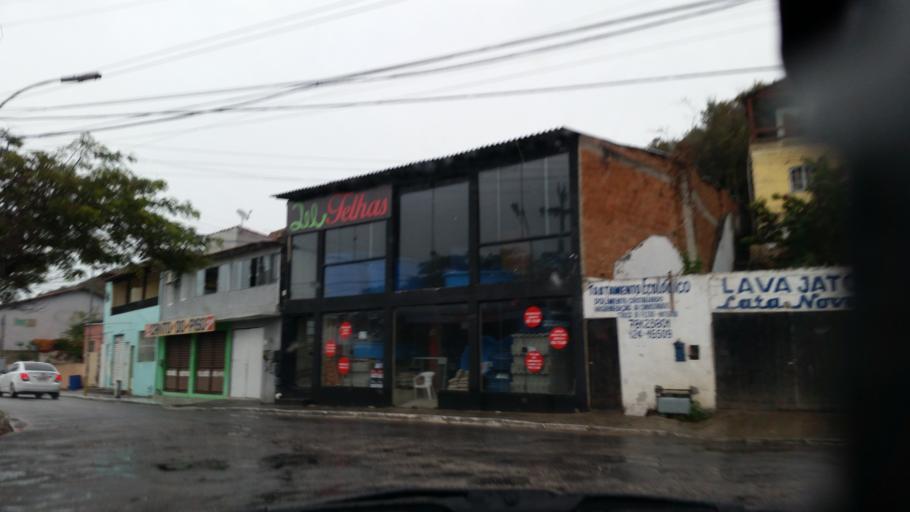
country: BR
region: Rio de Janeiro
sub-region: Cabo Frio
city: Cabo Frio
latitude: -22.8664
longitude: -42.0149
